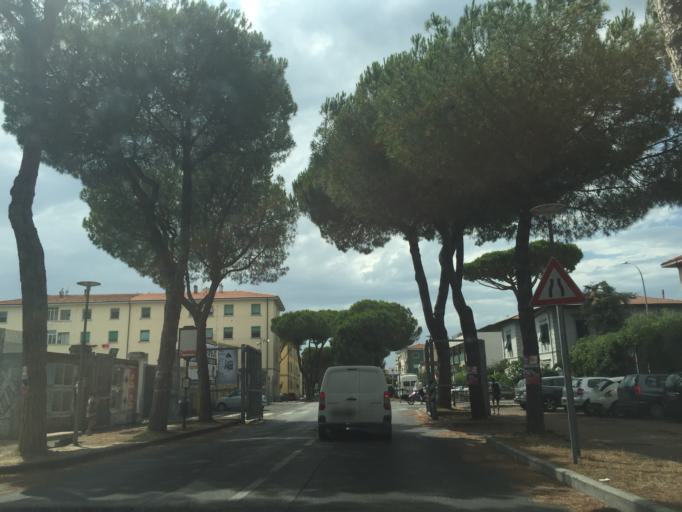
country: IT
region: Tuscany
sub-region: Province of Pisa
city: Pisa
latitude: 43.7265
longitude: 10.4002
